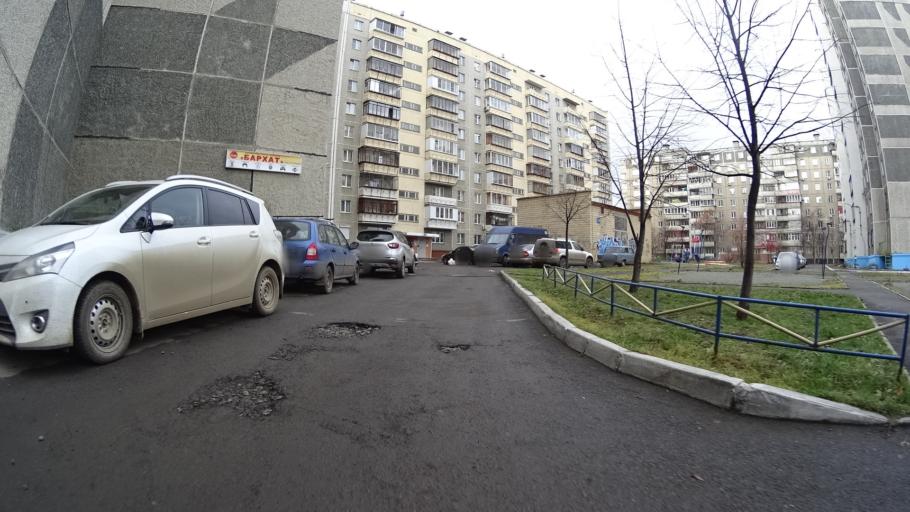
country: RU
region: Chelyabinsk
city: Roshchino
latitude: 55.1844
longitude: 61.2918
